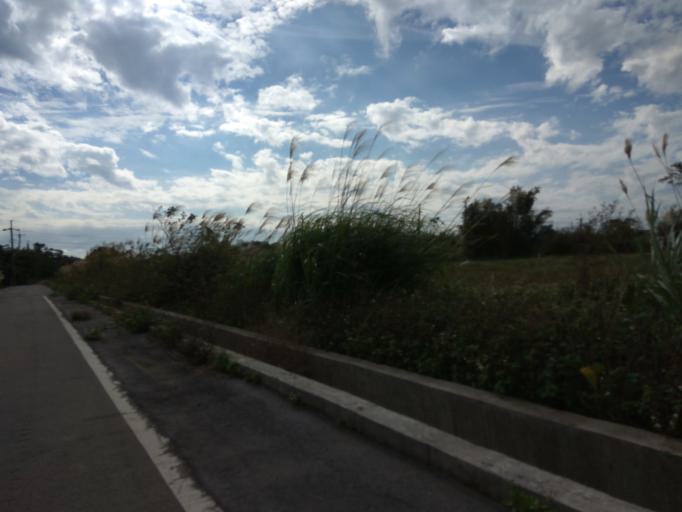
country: TW
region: Taiwan
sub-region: Hsinchu
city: Zhubei
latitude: 24.9578
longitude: 121.1052
